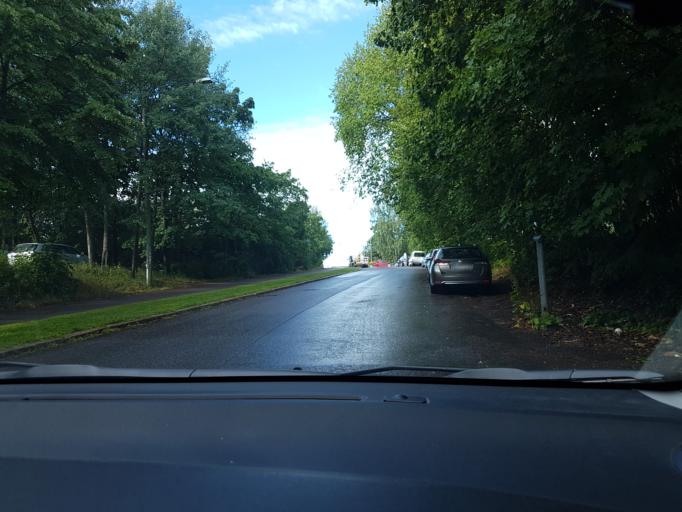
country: FI
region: Uusimaa
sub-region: Helsinki
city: Vantaa
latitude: 60.2370
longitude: 25.0183
